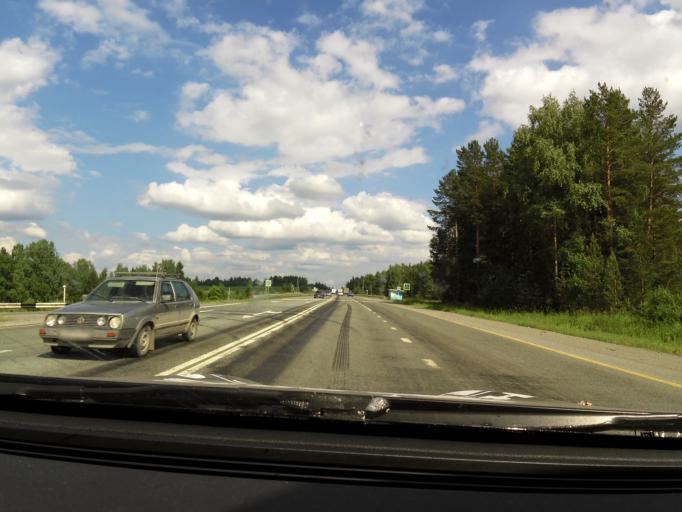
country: RU
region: Sverdlovsk
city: Bisert'
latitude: 56.8291
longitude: 59.0632
